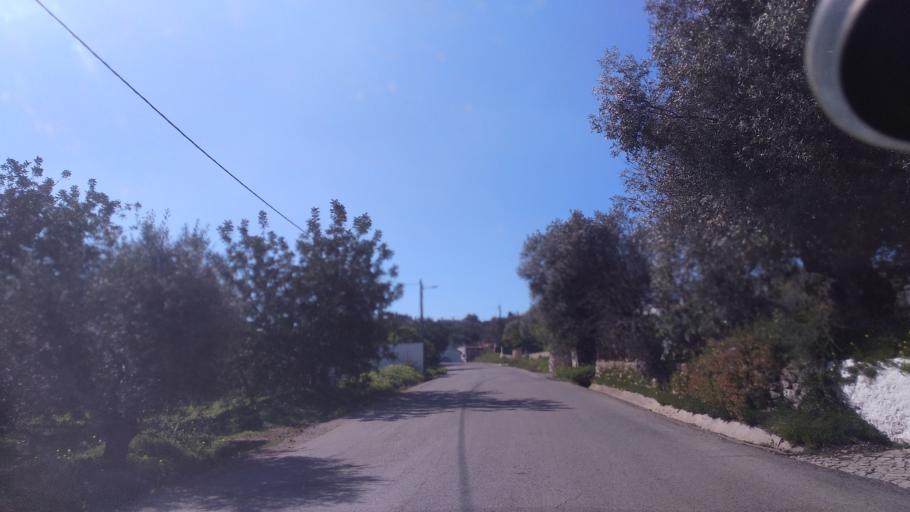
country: PT
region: Faro
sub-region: Faro
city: Santa Barbara de Nexe
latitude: 37.1187
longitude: -7.9257
